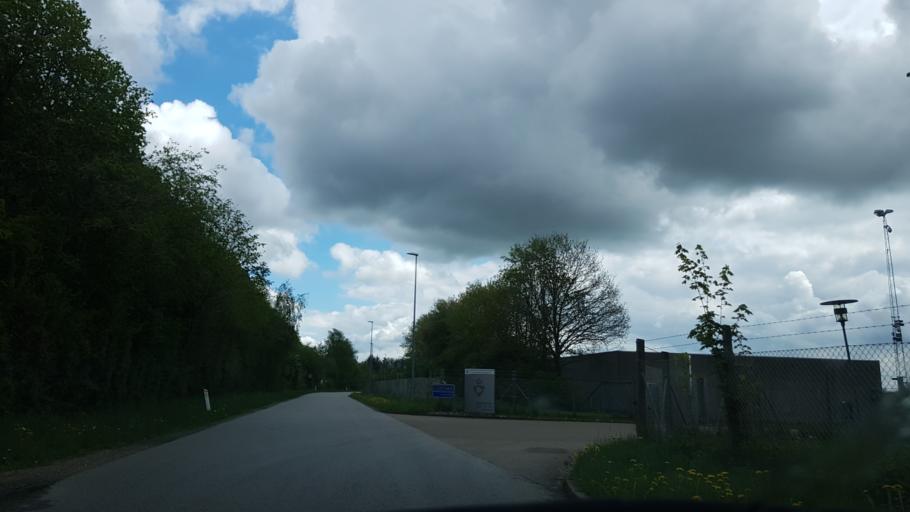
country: DK
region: South Denmark
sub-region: Haderslev Kommune
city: Vojens
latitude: 55.2354
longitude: 9.2674
